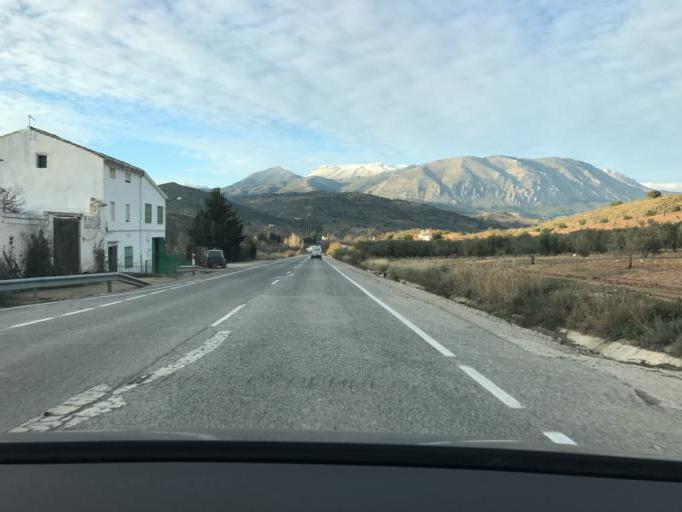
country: ES
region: Andalusia
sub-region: Provincia de Jaen
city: Huelma
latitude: 37.6429
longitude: -3.4167
